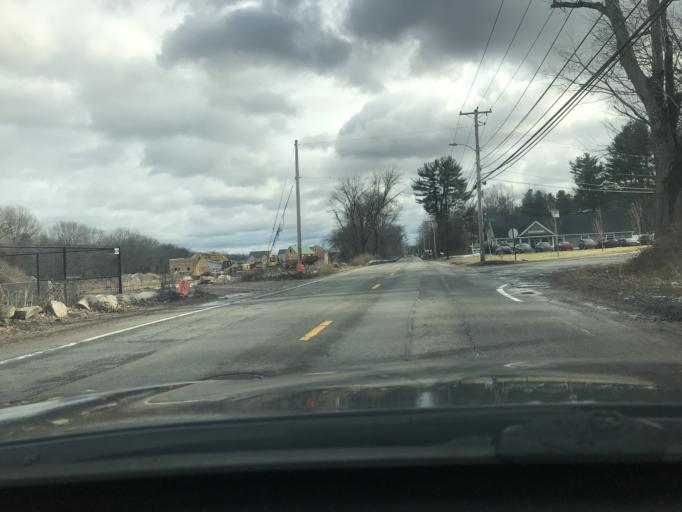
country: US
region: Massachusetts
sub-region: Middlesex County
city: Tyngsboro
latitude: 42.6679
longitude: -71.4140
